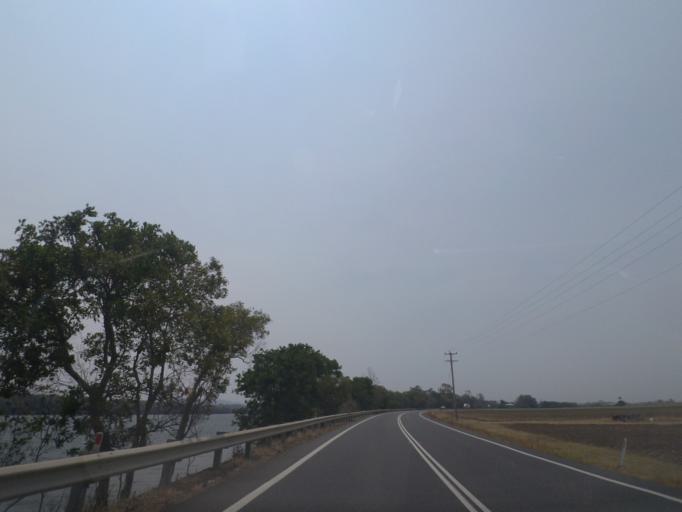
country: AU
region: New South Wales
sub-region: Richmond Valley
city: Evans Head
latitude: -28.9743
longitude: 153.4610
